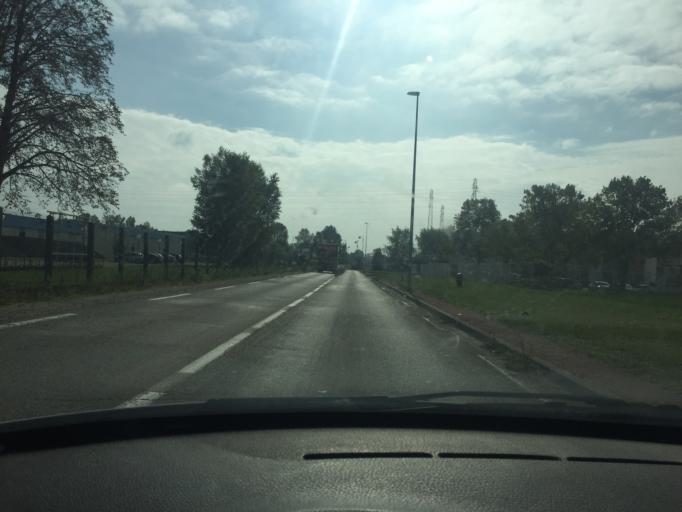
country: FR
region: Rhone-Alpes
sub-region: Departement de l'Ain
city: Saint-Maurice-de-Beynost
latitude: 45.8232
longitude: 4.9890
